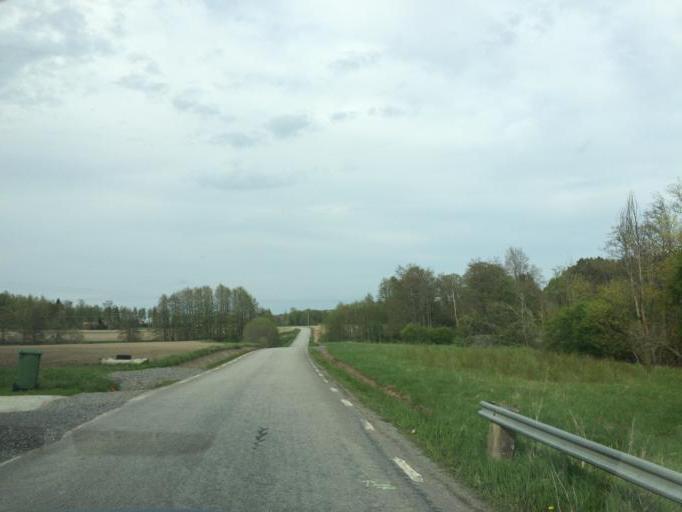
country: SE
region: Vaestmanland
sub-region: Kopings Kommun
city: Koping
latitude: 59.5882
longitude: 15.9875
